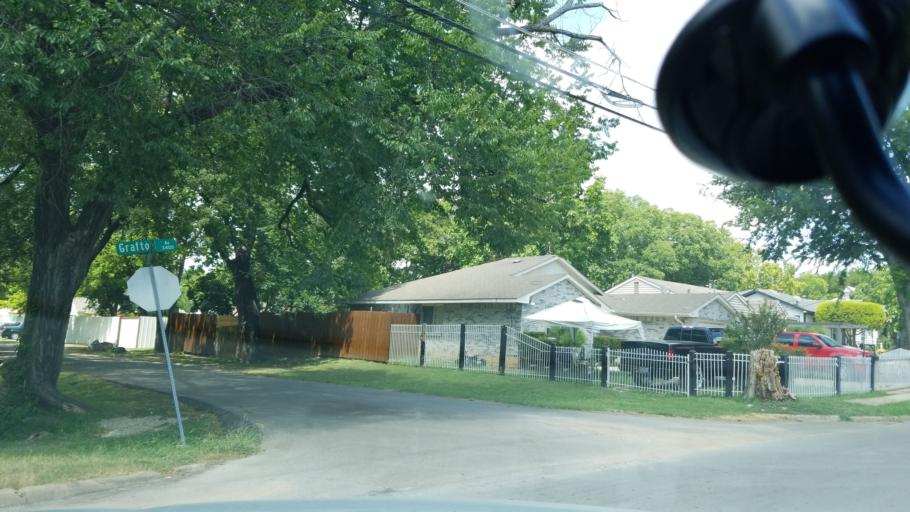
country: US
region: Texas
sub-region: Dallas County
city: Cockrell Hill
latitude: 32.7302
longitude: -96.8778
